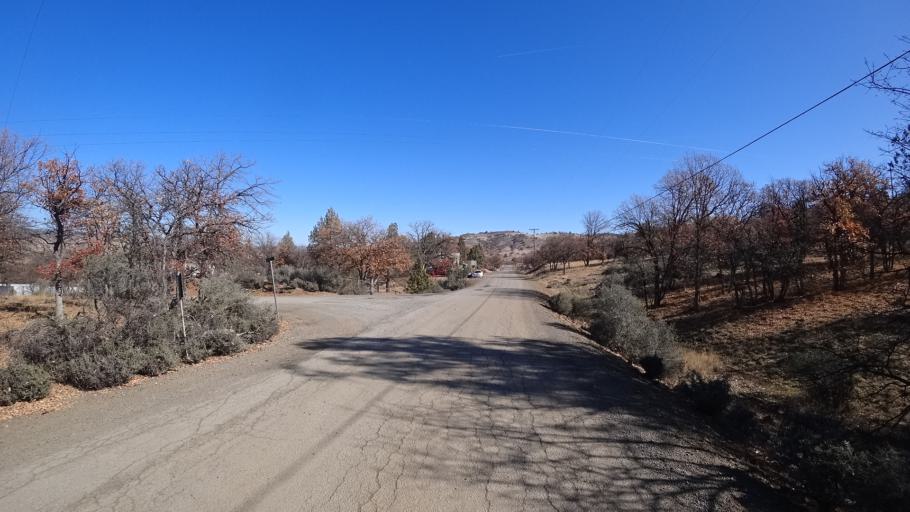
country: US
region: California
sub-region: Siskiyou County
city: Montague
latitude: 41.8838
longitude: -122.4911
